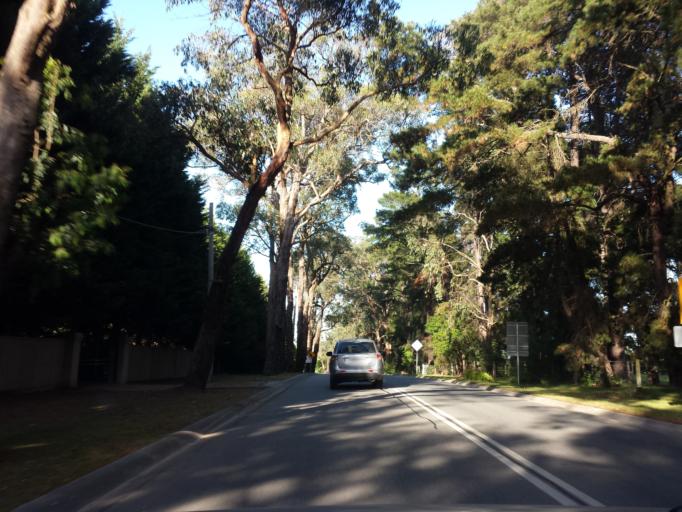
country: AU
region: Victoria
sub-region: Casey
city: Narre Warren North
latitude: -37.9954
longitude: 145.3480
